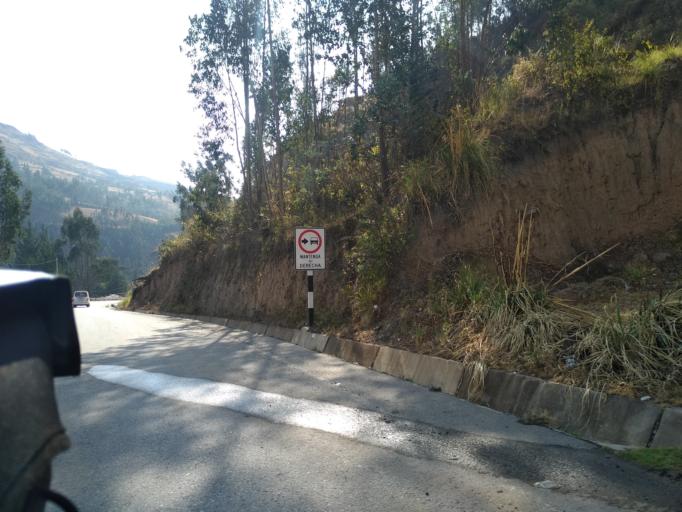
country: PE
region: La Libertad
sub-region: Provincia de Otuzco
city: Mache
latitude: -7.9977
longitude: -78.5045
